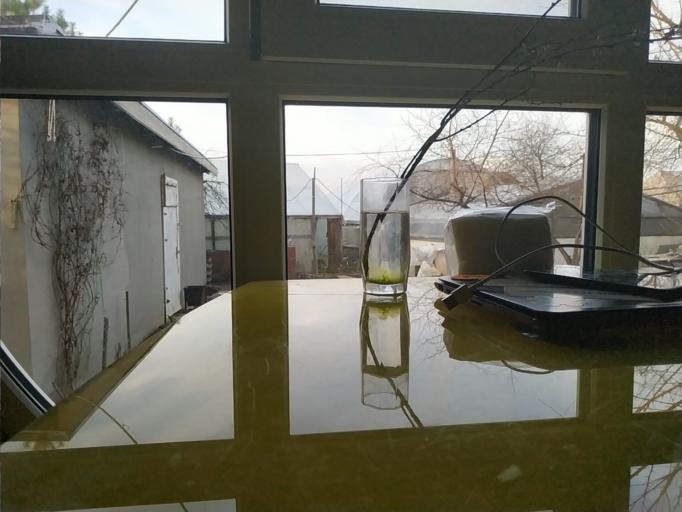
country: RU
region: Republic of Karelia
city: Suoyarvi
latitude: 62.1834
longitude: 32.1258
